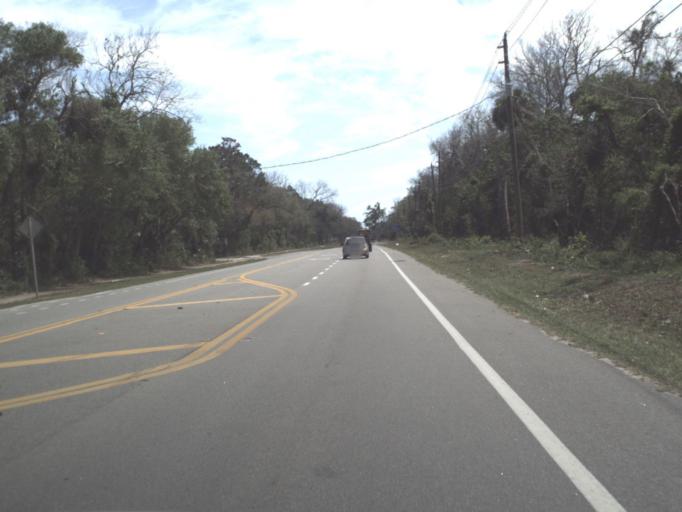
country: US
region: Florida
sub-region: Flagler County
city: Palm Coast
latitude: 29.5874
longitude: -81.1904
